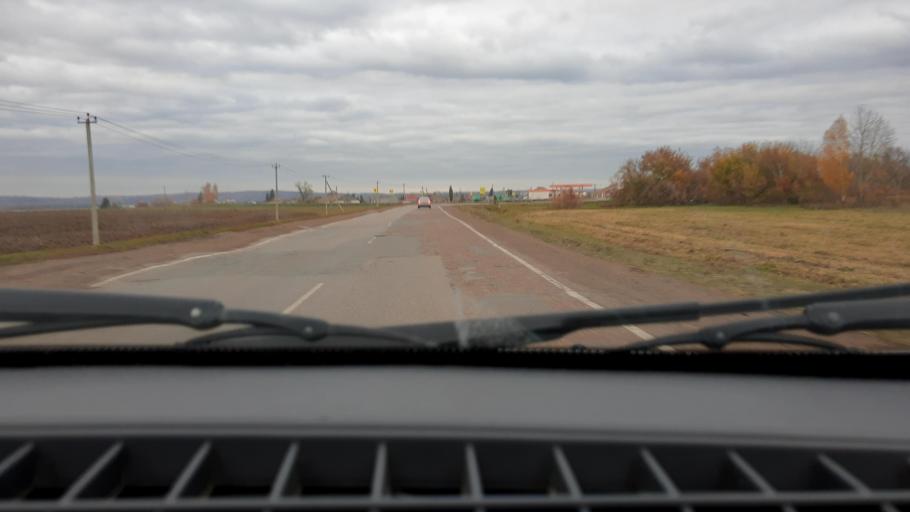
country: RU
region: Bashkortostan
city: Kabakovo
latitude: 54.5459
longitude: 56.0834
